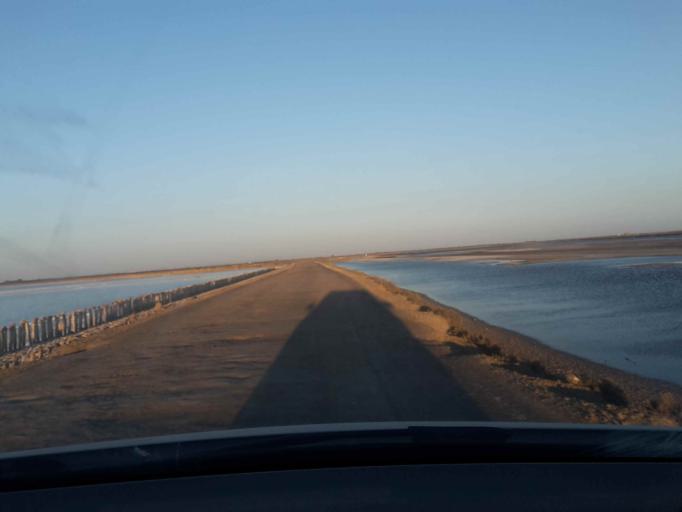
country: FR
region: Provence-Alpes-Cote d'Azur
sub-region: Departement des Bouches-du-Rhone
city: Port-Saint-Louis-du-Rhone
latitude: 43.4137
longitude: 4.6363
